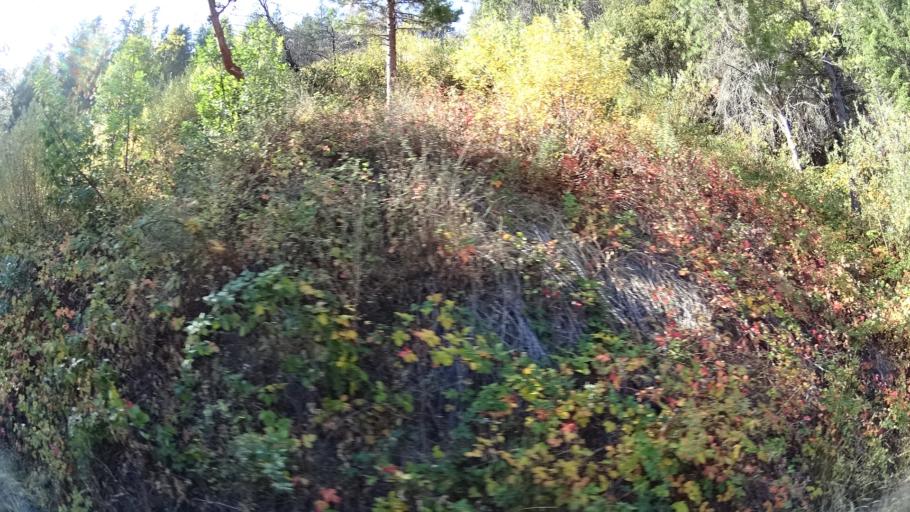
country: US
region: California
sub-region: Siskiyou County
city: Happy Camp
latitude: 41.7673
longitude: -123.0264
